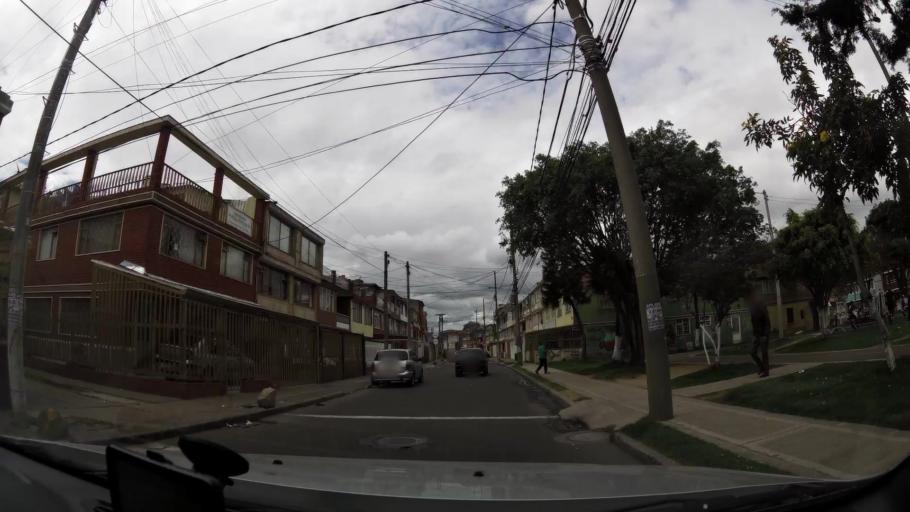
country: CO
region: Bogota D.C.
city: Bogota
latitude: 4.6190
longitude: -74.1112
